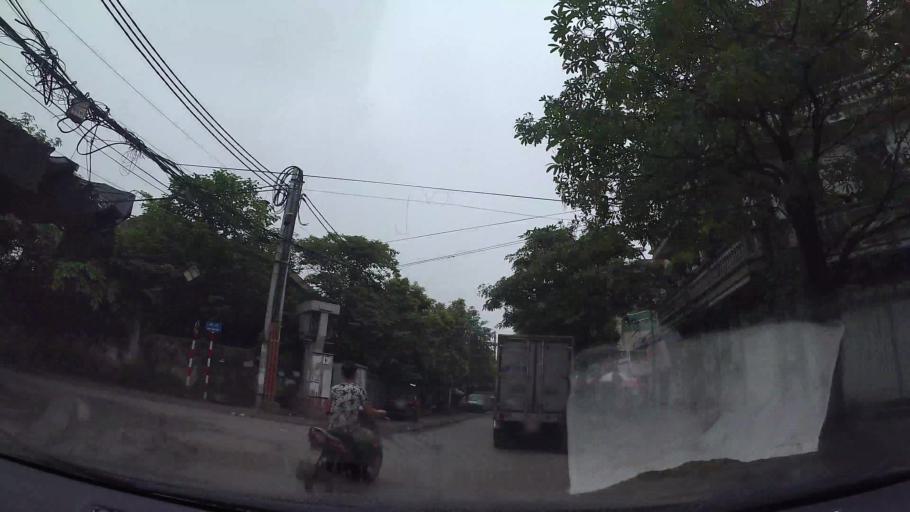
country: VN
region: Ha Noi
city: Hai BaTrung
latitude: 20.9789
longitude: 105.8841
